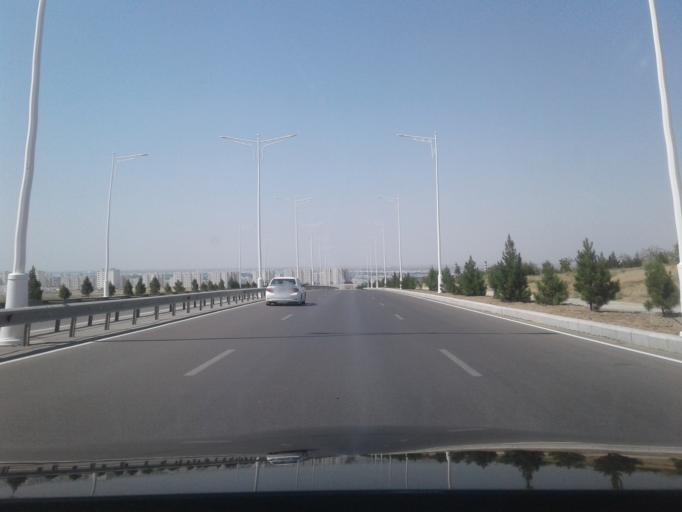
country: TM
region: Ahal
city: Ashgabat
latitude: 37.8846
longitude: 58.4225
